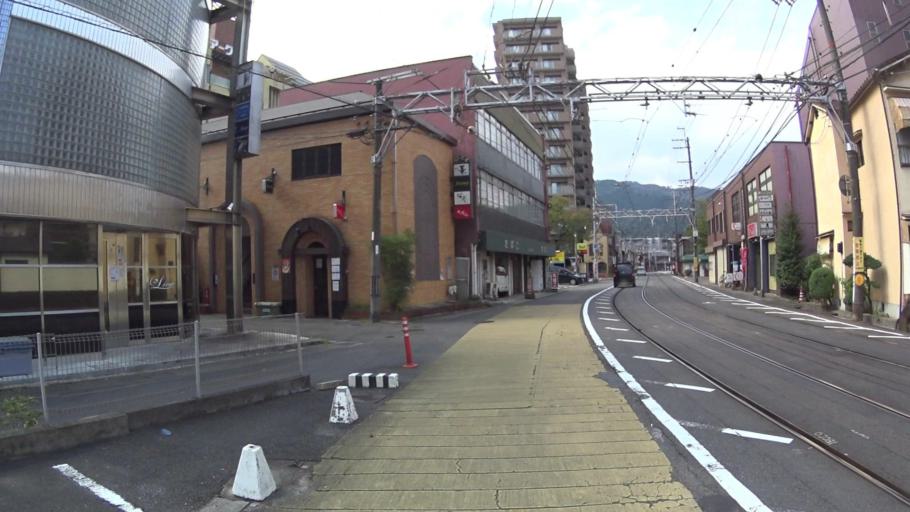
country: JP
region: Shiga Prefecture
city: Nagahama
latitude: 35.3859
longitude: 136.2248
